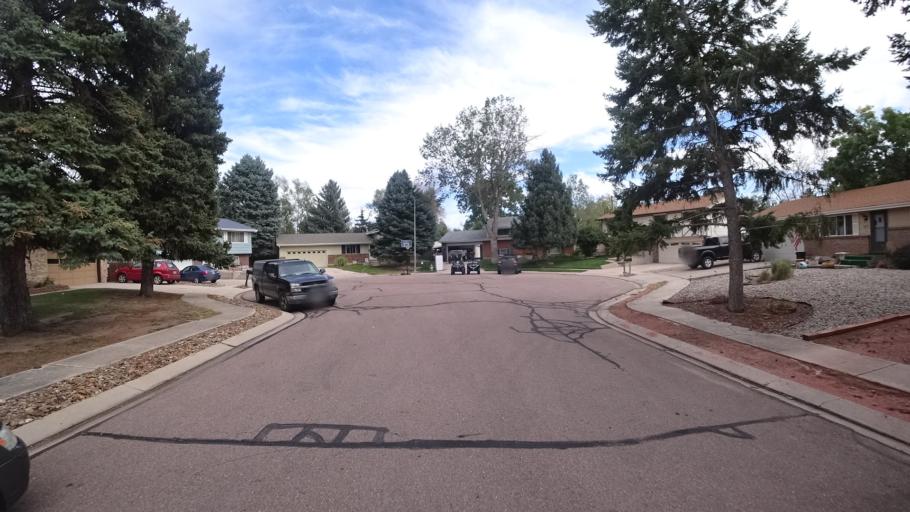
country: US
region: Colorado
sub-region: El Paso County
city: Colorado Springs
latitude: 38.9002
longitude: -104.7734
